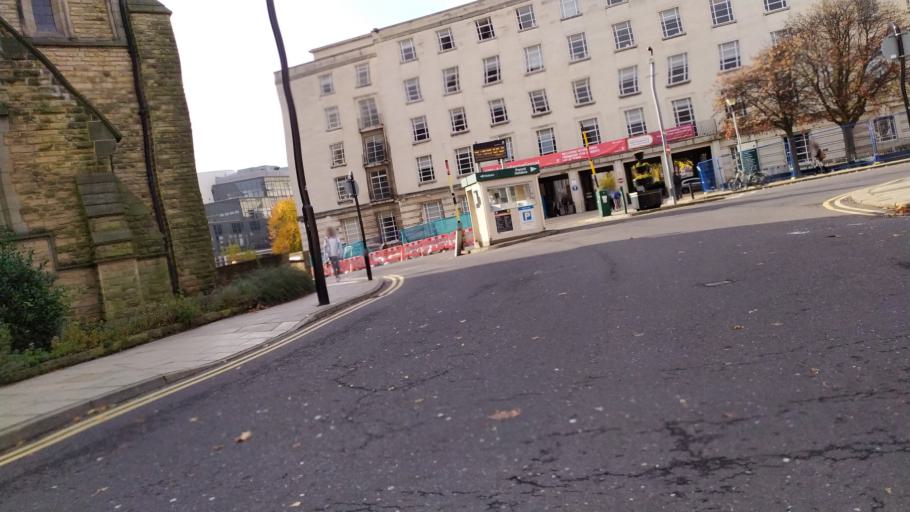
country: GB
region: England
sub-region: City and Borough of Leeds
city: Leeds
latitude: 53.8074
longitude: -1.5521
